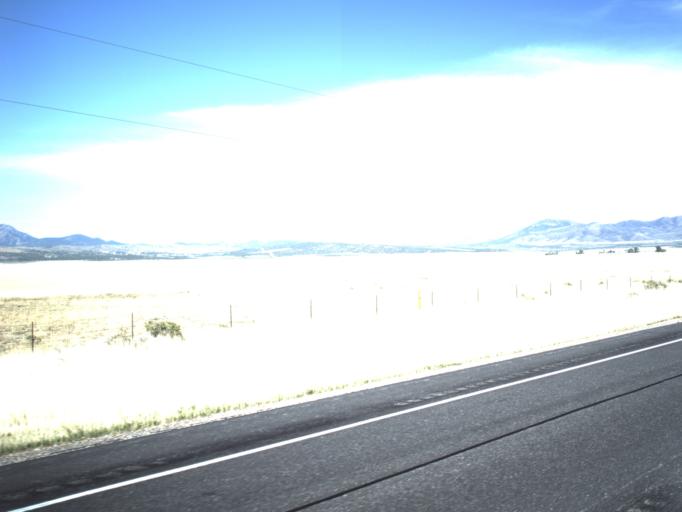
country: US
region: Utah
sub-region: Millard County
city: Fillmore
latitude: 39.1181
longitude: -112.3307
